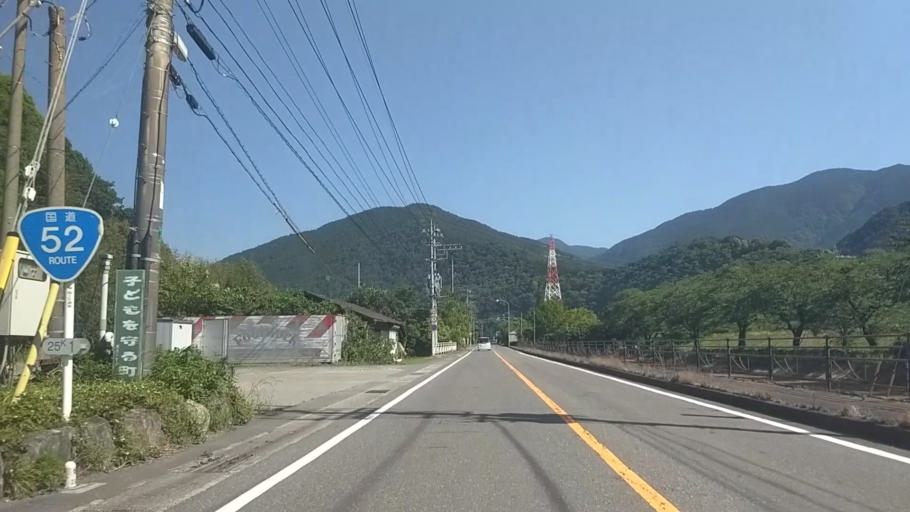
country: JP
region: Shizuoka
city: Fujinomiya
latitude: 35.2326
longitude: 138.5073
